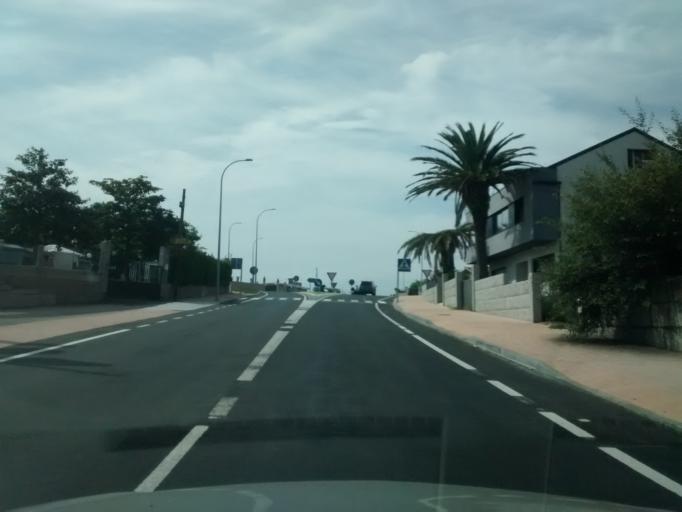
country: ES
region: Galicia
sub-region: Provincia de Pontevedra
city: Sanxenxo
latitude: 42.4214
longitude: -8.8732
